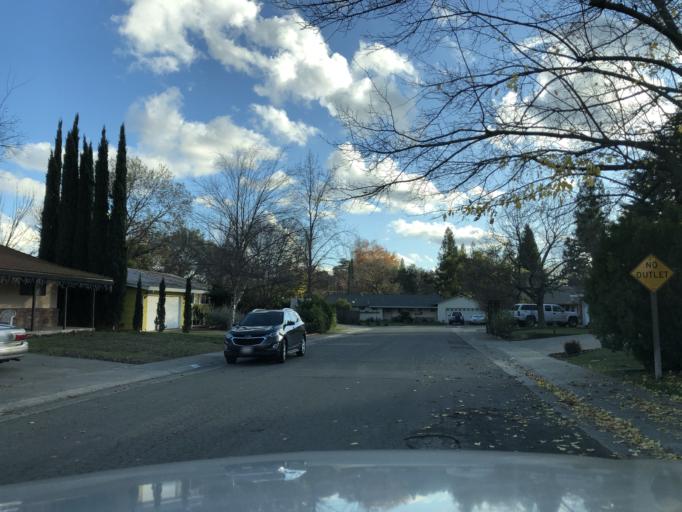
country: US
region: California
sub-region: Sacramento County
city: Foothill Farms
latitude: 38.6581
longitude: -121.3227
